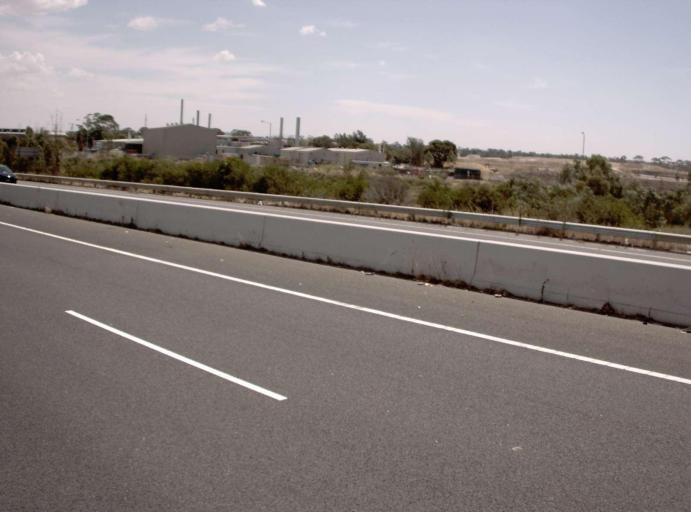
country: AU
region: Victoria
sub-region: Darebin
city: Reservoir
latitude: -37.6897
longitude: 144.9835
